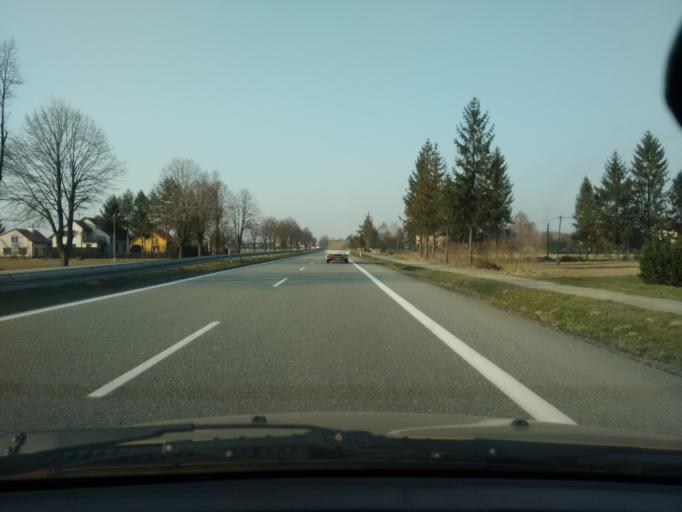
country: PL
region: Silesian Voivodeship
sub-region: Powiat cieszynski
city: Drogomysl
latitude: 49.8748
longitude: 18.7437
